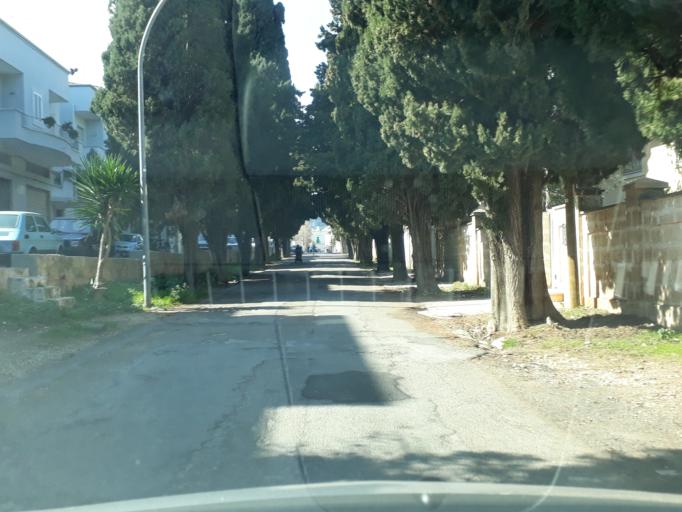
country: IT
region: Apulia
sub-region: Provincia di Brindisi
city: Fasano
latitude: 40.8385
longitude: 17.3646
